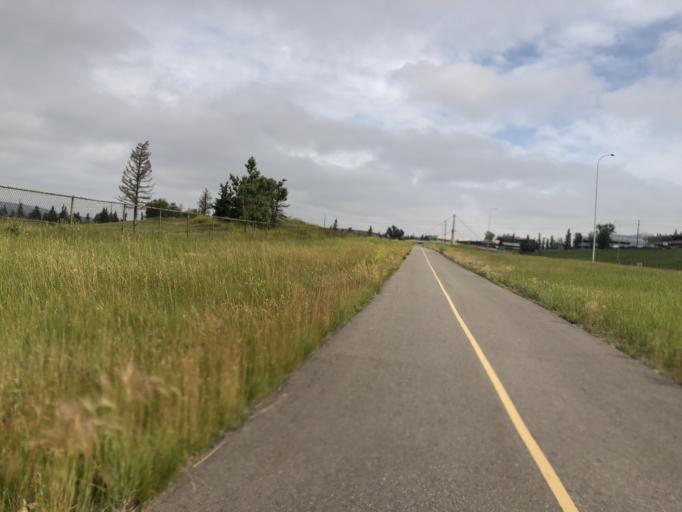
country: CA
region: Alberta
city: Calgary
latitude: 51.0714
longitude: -114.0275
